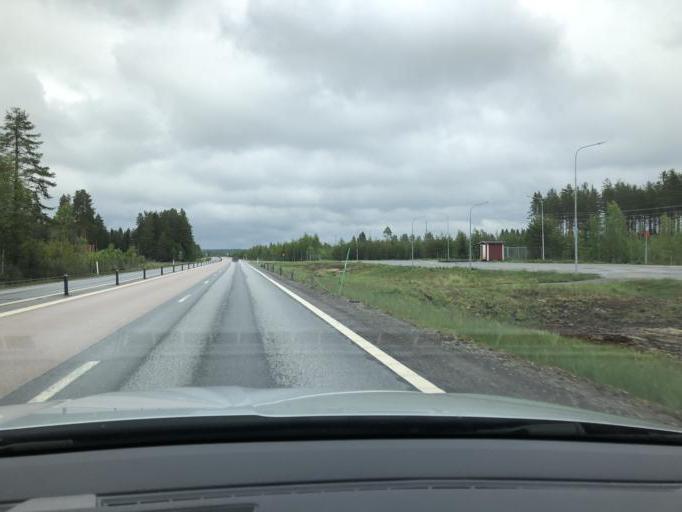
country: SE
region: Vaesterbotten
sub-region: Nordmalings Kommun
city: Nordmaling
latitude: 63.5544
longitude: 19.4205
